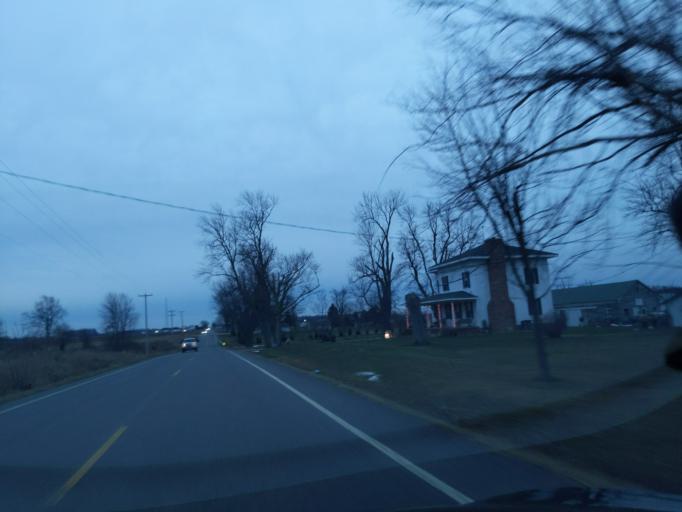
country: US
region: Michigan
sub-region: Ionia County
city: Portland
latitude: 42.8811
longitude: -84.9560
